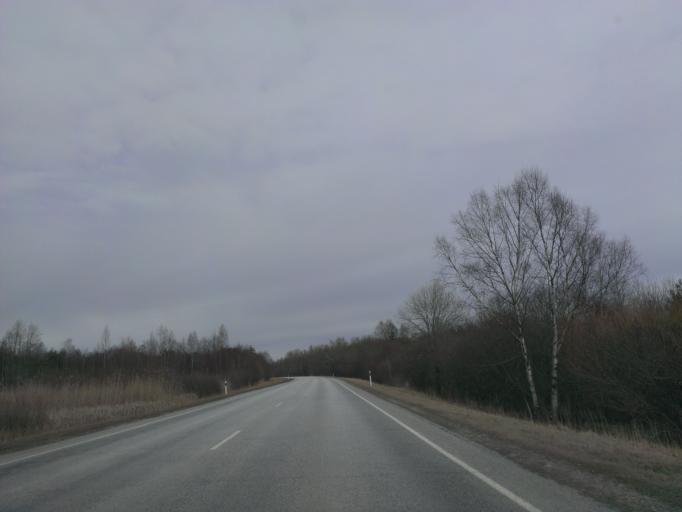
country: EE
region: Laeaene
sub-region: Lihula vald
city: Lihula
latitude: 58.5970
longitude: 23.5487
